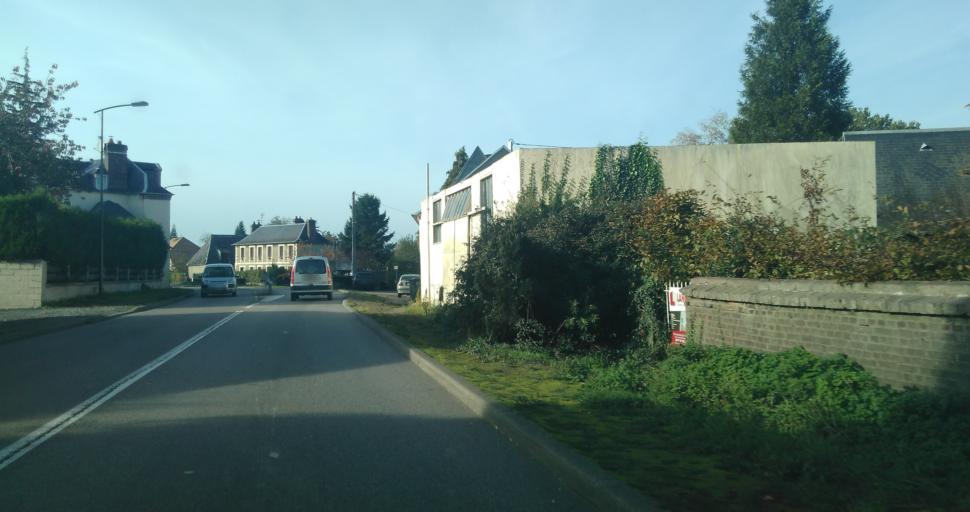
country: FR
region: Haute-Normandie
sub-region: Departement de l'Eure
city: Caumont
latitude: 49.3527
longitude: 0.9152
